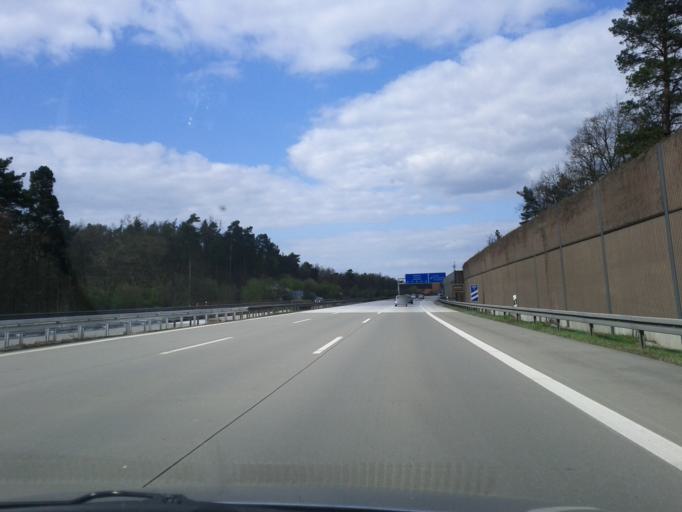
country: DE
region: Brandenburg
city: Grunheide
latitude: 52.4169
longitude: 13.7854
